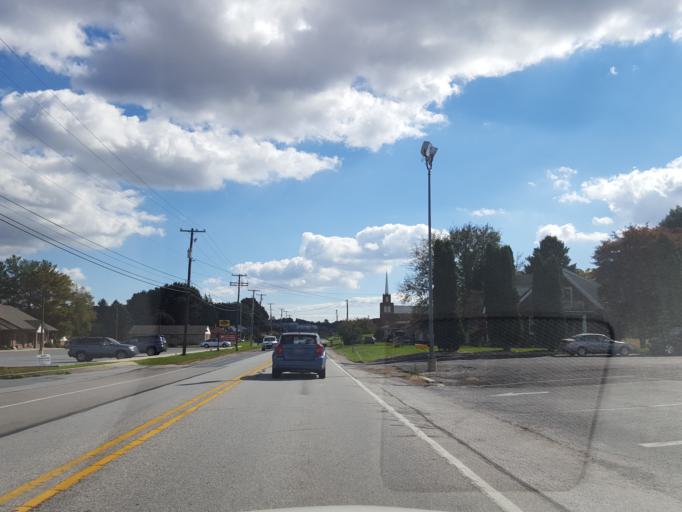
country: US
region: Pennsylvania
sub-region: York County
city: Yoe
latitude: 39.9250
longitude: -76.6357
